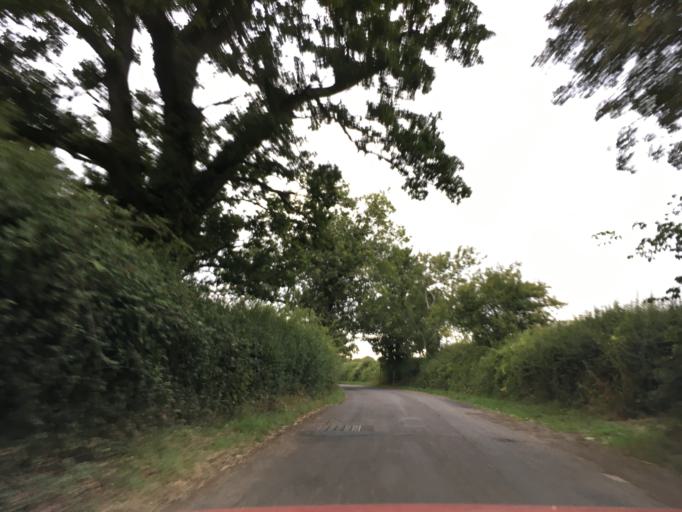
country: GB
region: England
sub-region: Wiltshire
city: Biddestone
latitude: 51.4517
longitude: -2.1987
